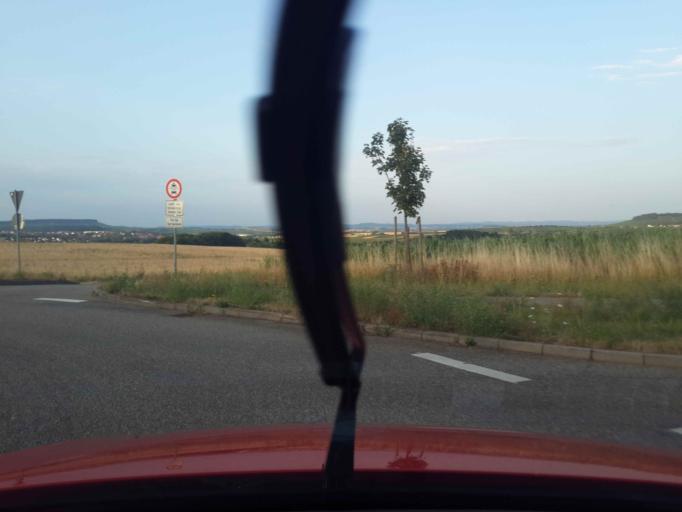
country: DE
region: Baden-Wuerttemberg
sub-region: Regierungsbezirk Stuttgart
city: Guglingen
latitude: 49.0517
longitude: 8.9947
